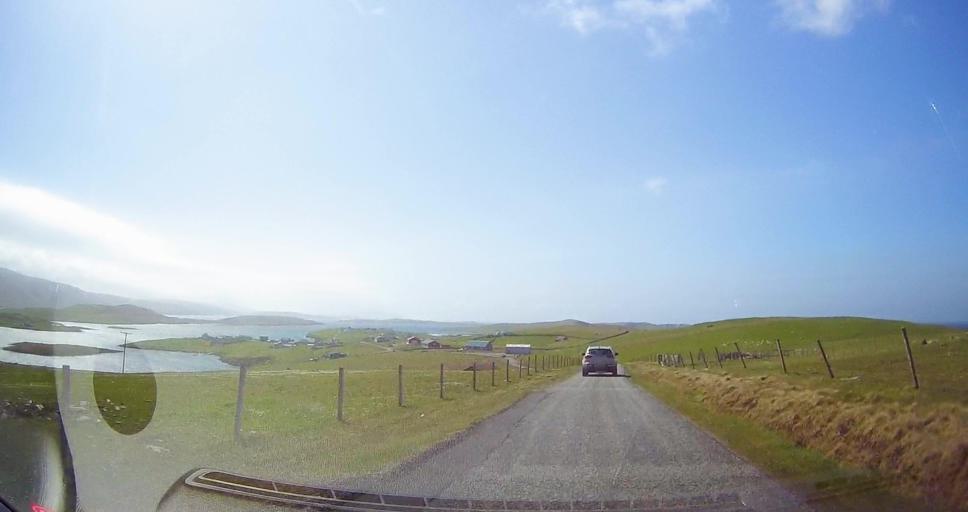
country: GB
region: Scotland
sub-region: Shetland Islands
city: Sandwick
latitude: 60.0741
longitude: -1.3384
